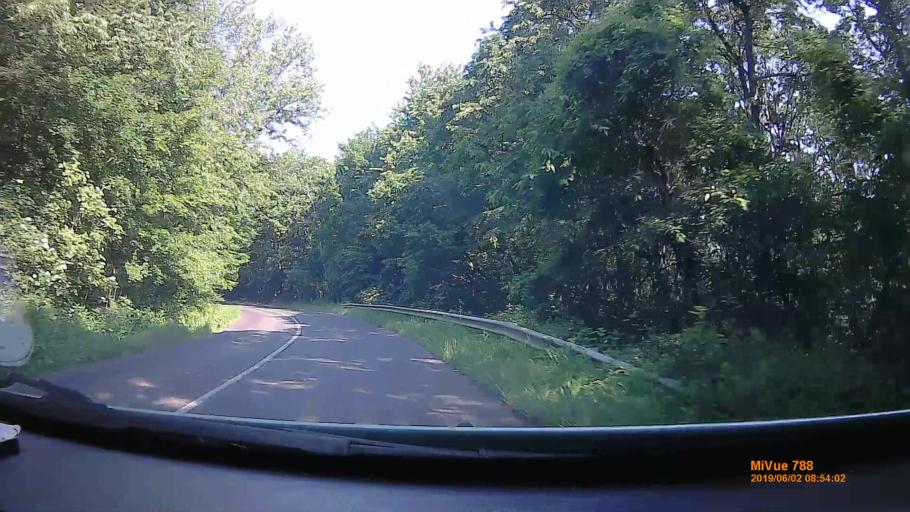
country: HU
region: Borsod-Abauj-Zemplen
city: Sajobabony
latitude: 48.1524
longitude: 20.6743
